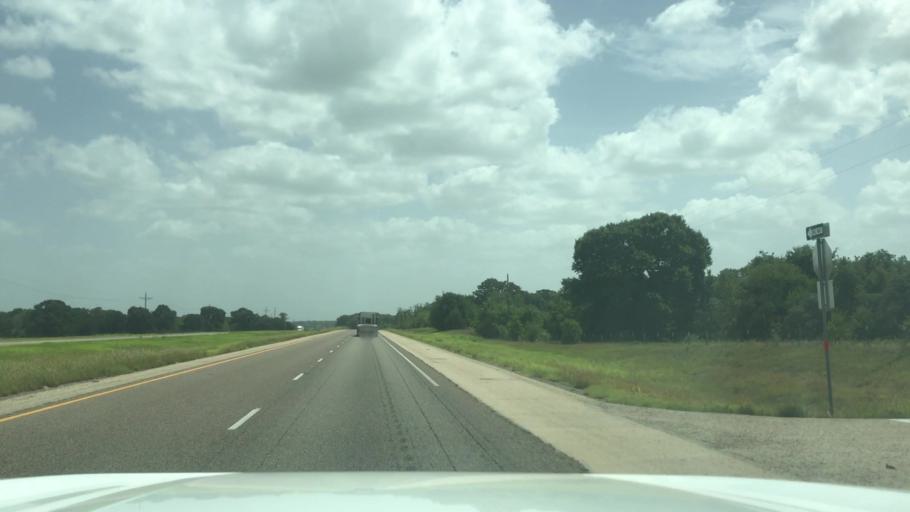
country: US
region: Texas
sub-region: Robertson County
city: Calvert
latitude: 31.0320
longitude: -96.7097
